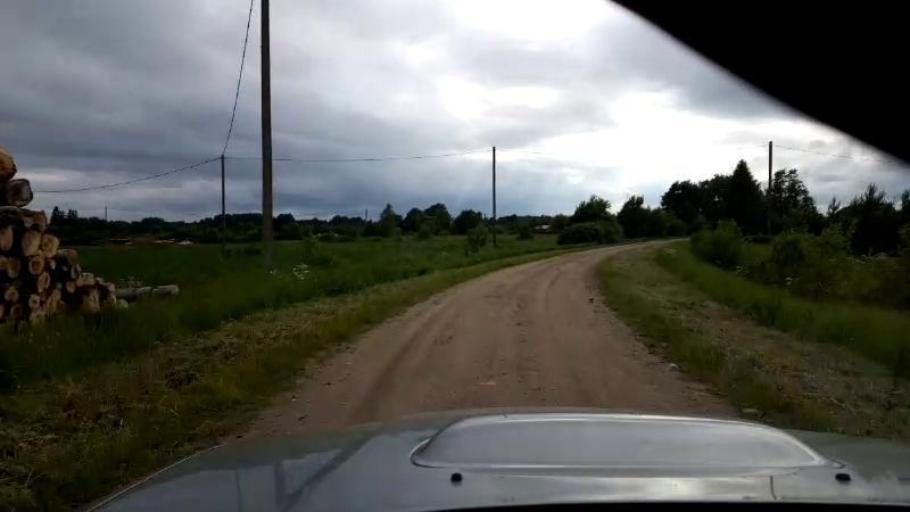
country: EE
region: Paernumaa
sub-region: Halinga vald
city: Parnu-Jaagupi
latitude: 58.5628
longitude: 24.5757
